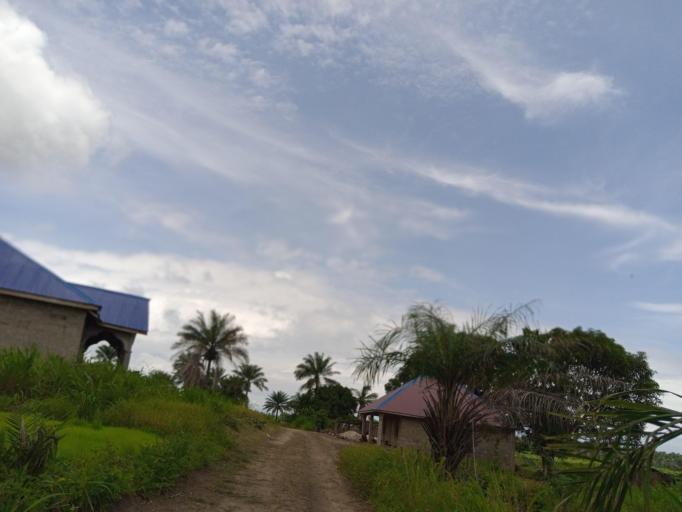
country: SL
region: Northern Province
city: Masoyila
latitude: 8.5902
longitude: -13.1712
